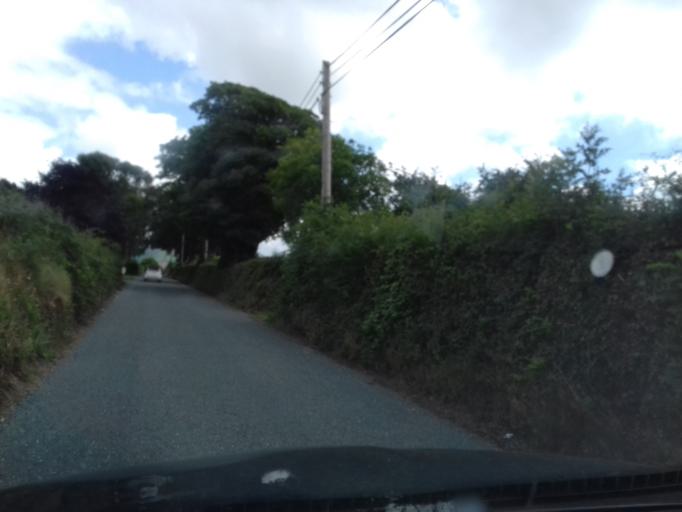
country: IE
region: Leinster
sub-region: Kilkenny
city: Graiguenamanagh
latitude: 52.6119
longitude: -6.8496
